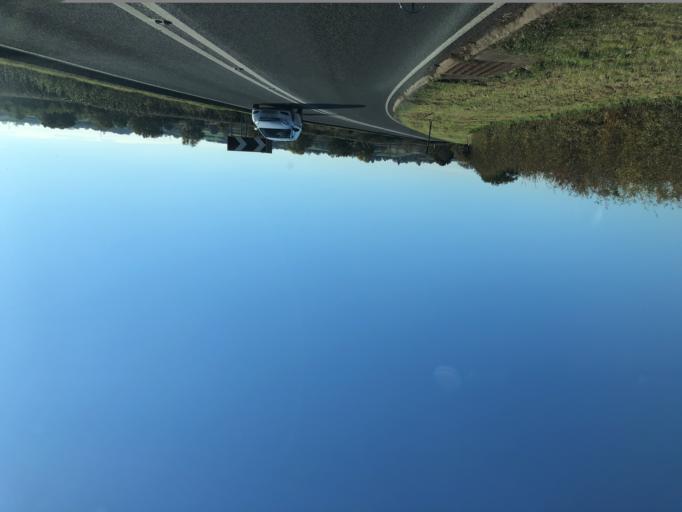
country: GB
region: England
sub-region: Warwickshire
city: Harbury
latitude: 52.2662
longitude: -1.4682
